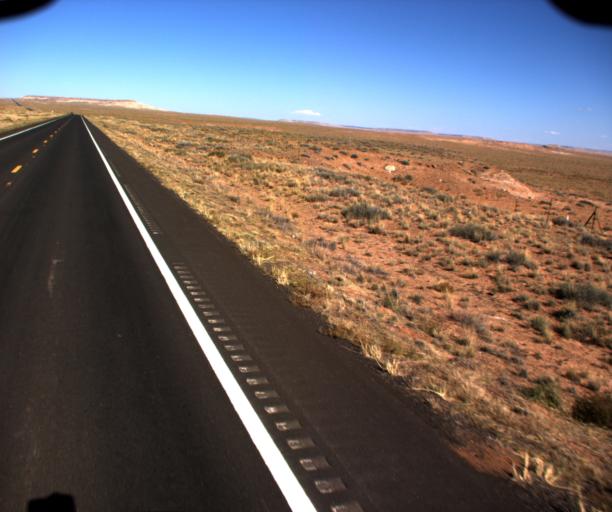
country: US
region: Arizona
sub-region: Coconino County
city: Tuba City
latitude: 36.1766
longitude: -111.0807
